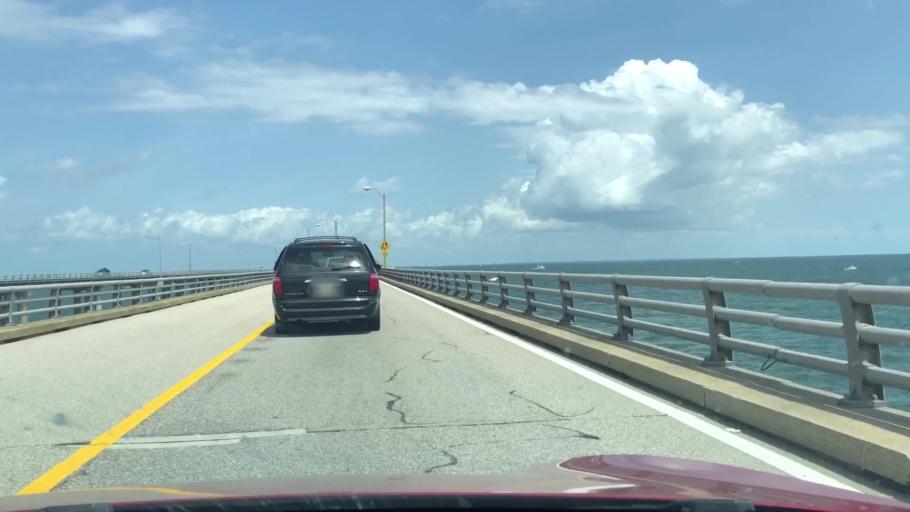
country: US
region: Virginia
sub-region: City of Virginia Beach
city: Virginia Beach
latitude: 36.9586
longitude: -76.1155
